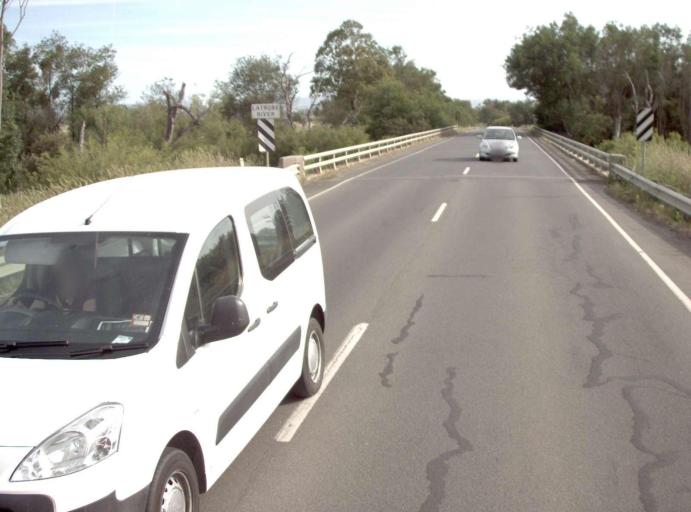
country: AU
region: Victoria
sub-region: Latrobe
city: Traralgon
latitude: -38.1522
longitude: 146.5542
